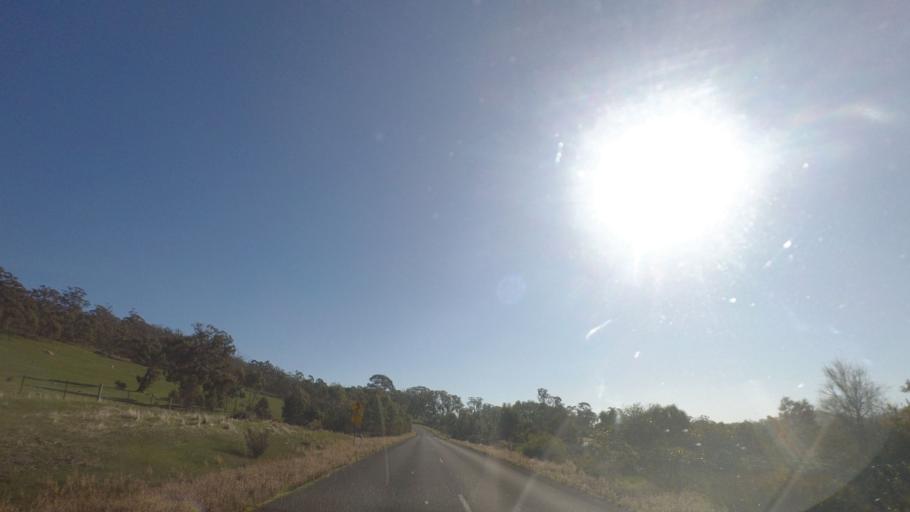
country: AU
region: Victoria
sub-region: Mount Alexander
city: Castlemaine
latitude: -37.0363
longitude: 144.2773
